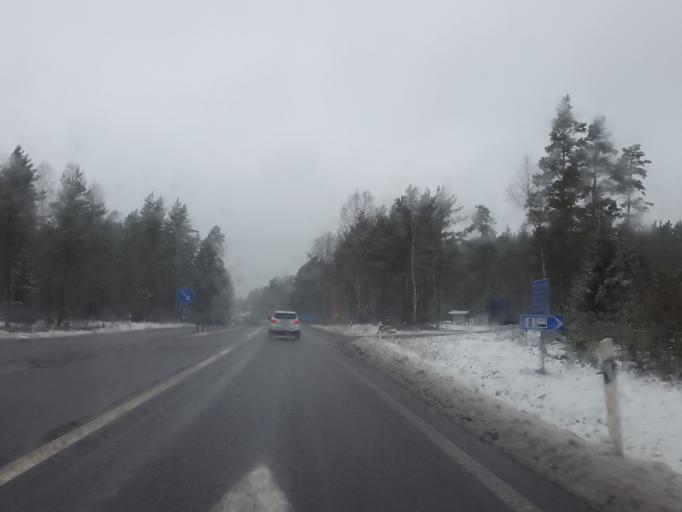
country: SE
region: Joenkoeping
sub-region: Mullsjo Kommun
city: Mullsjoe
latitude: 57.7618
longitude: 13.8339
